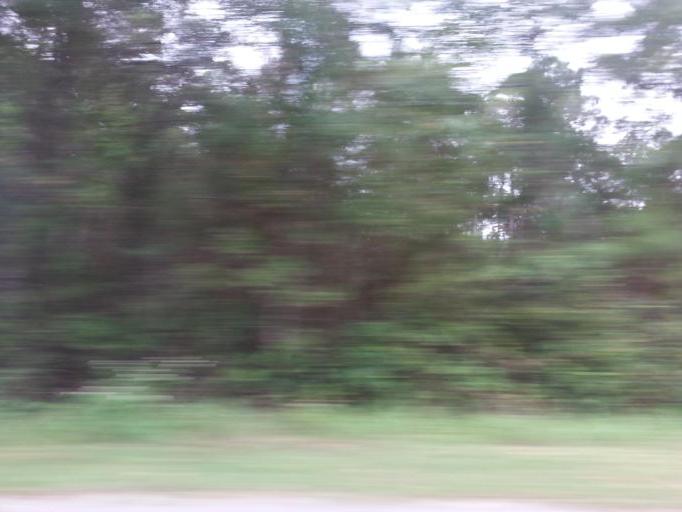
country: US
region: Alabama
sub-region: Baldwin County
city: Point Clear
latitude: 30.4942
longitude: -87.9250
